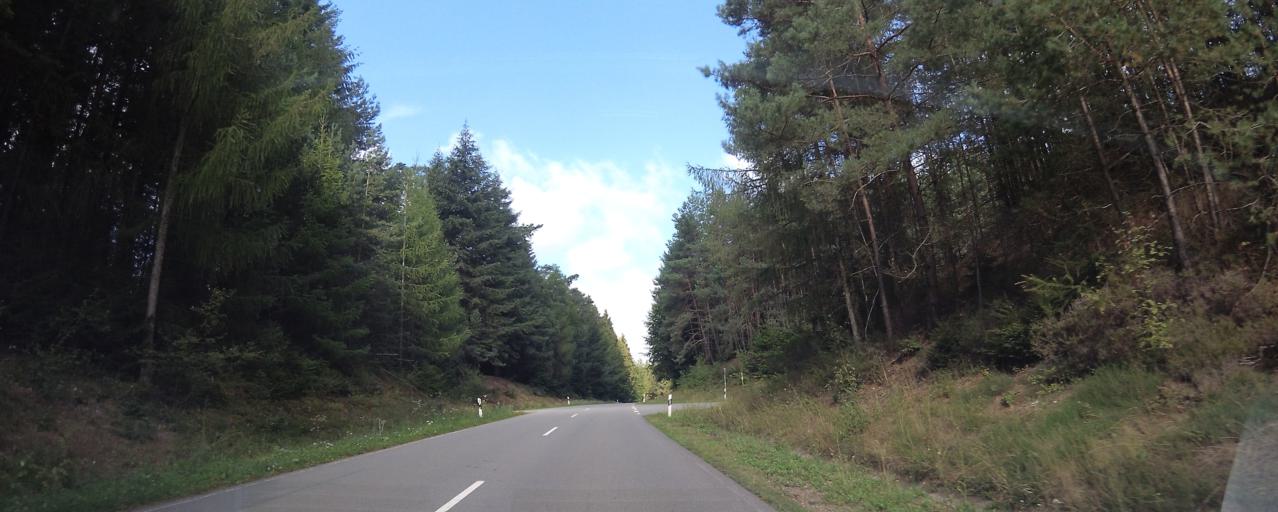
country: DE
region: Rheinland-Pfalz
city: Dierscheid
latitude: 49.8803
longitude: 6.7322
